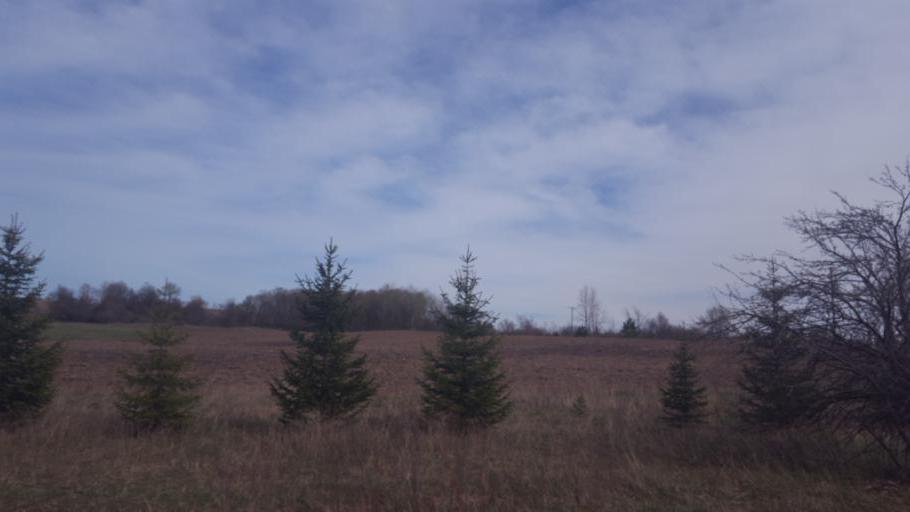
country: US
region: Michigan
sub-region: Gladwin County
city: Gladwin
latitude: 43.9748
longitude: -84.5453
